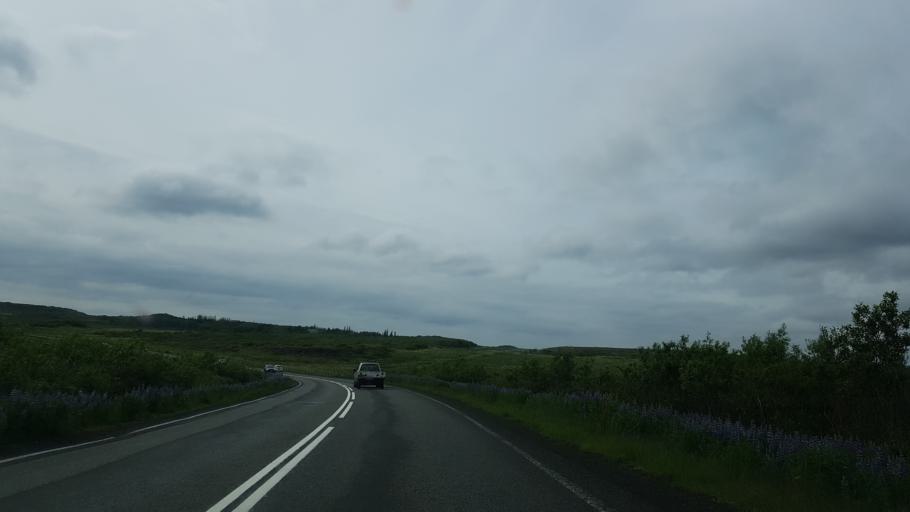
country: IS
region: West
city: Borgarnes
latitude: 64.6578
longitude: -21.7245
